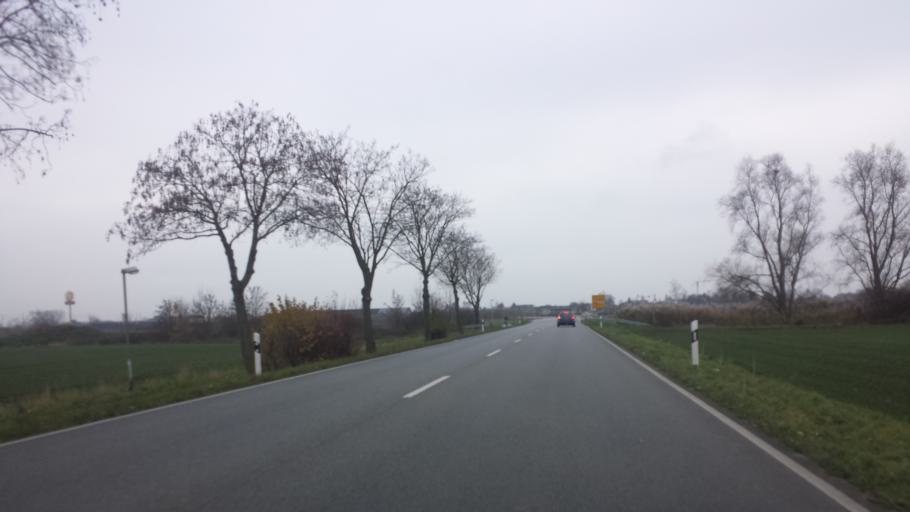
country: DE
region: Hesse
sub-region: Regierungsbezirk Darmstadt
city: Burstadt
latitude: 49.6581
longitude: 8.4502
